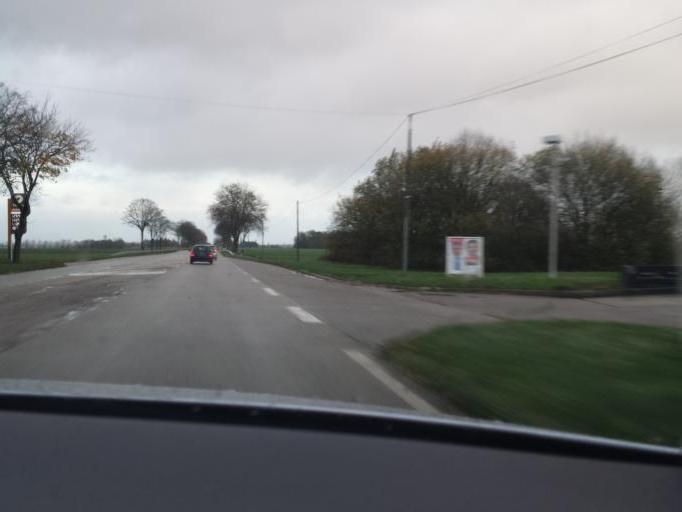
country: FR
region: Ile-de-France
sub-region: Departement des Yvelines
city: Bennecourt
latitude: 49.0202
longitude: 1.4896
